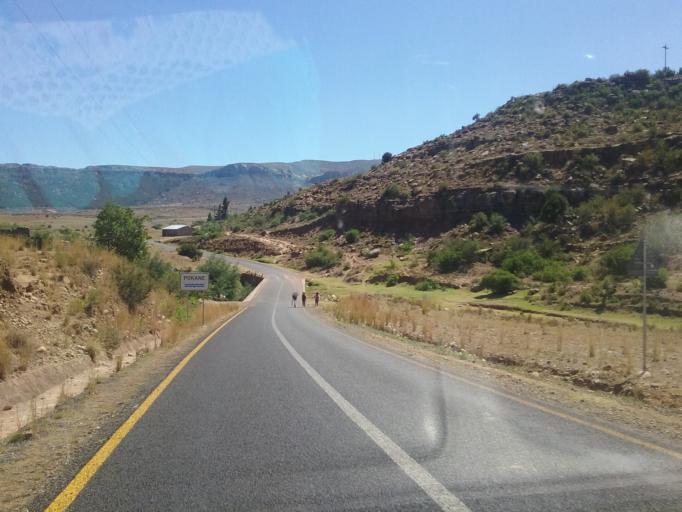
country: LS
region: Quthing
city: Quthing
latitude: -30.3341
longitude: 27.7441
